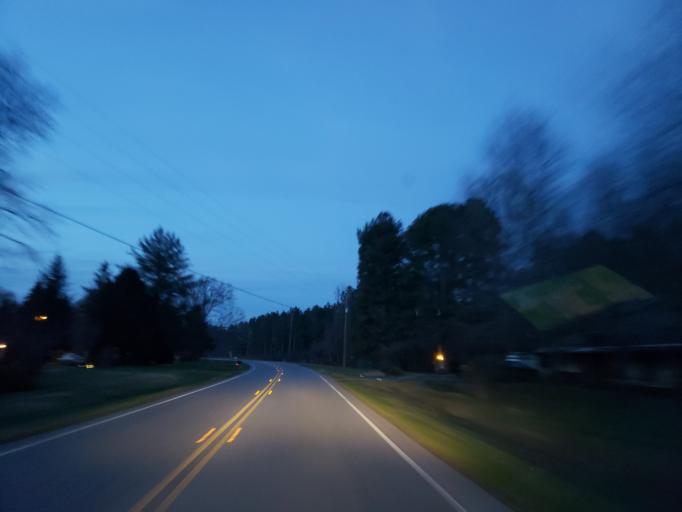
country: US
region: Georgia
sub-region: Cherokee County
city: Ball Ground
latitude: 34.3322
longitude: -84.2646
